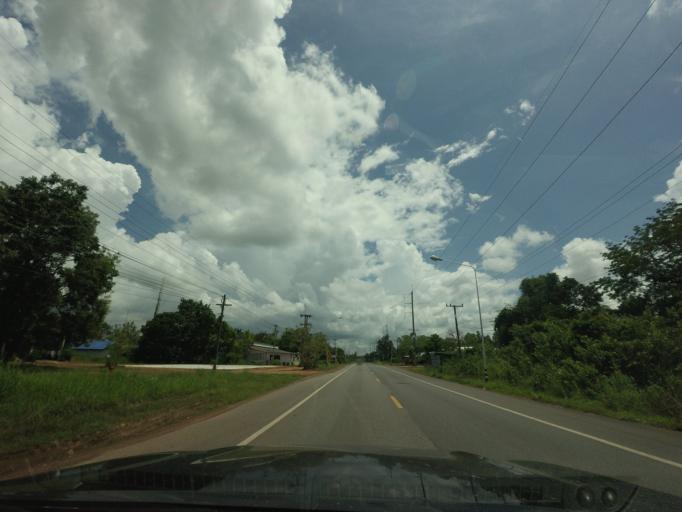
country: TH
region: Changwat Udon Thani
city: Udon Thani
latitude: 17.5343
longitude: 102.7659
